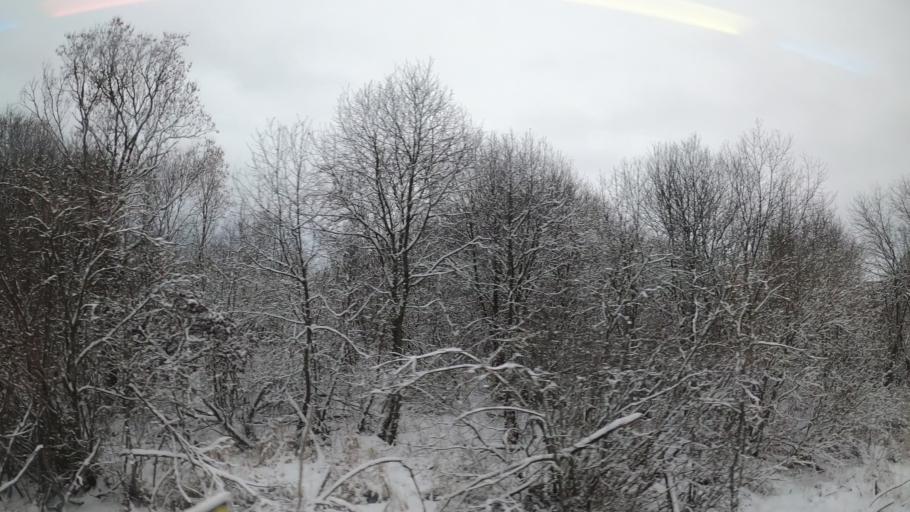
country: RU
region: Jaroslavl
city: Pereslavl'-Zalesskiy
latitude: 56.7141
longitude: 38.9106
